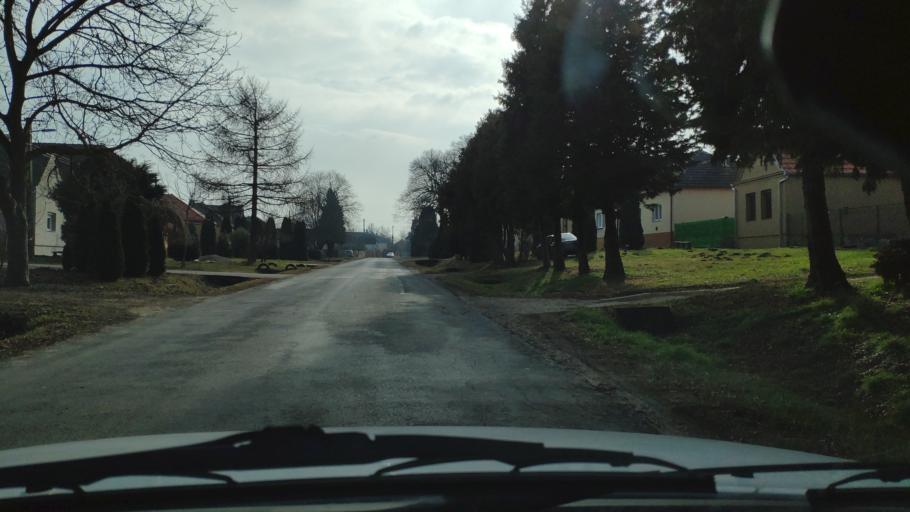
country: HU
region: Zala
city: Nagykanizsa
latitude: 46.4556
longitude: 16.9145
